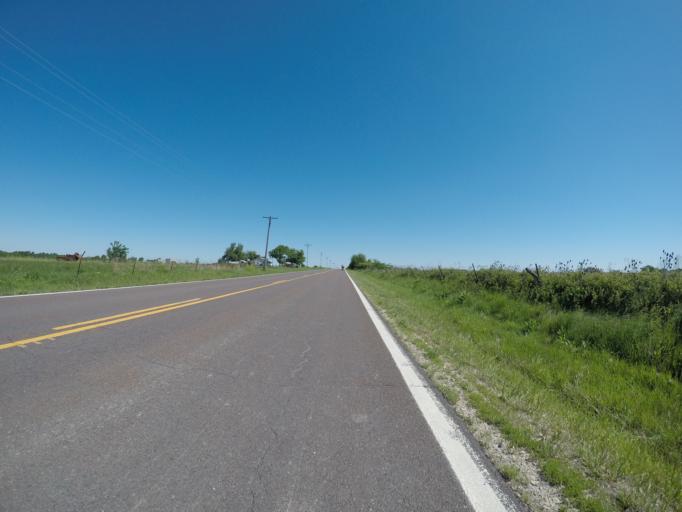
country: US
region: Kansas
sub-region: Wabaunsee County
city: Alma
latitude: 38.8005
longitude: -96.0946
